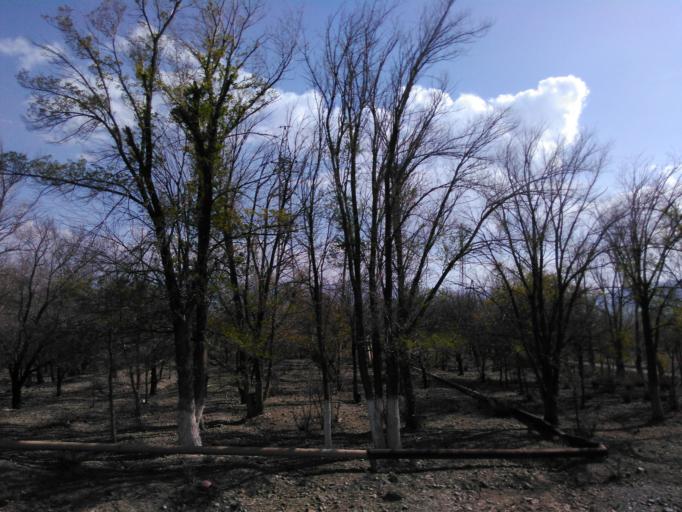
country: KG
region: Ysyk-Koel
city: Balykchy
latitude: 42.4546
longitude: 76.1552
